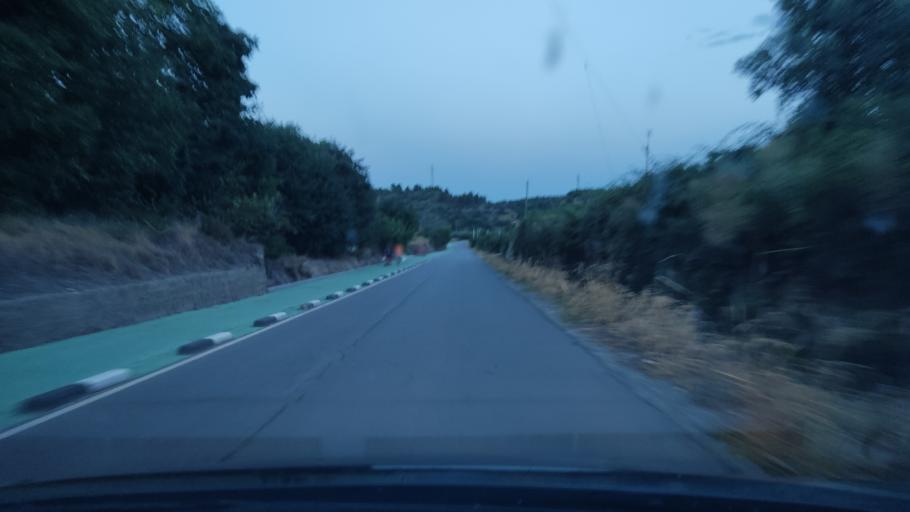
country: ES
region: Valencia
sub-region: Provincia de Castello
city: Jerica
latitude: 39.9097
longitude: -0.5656
